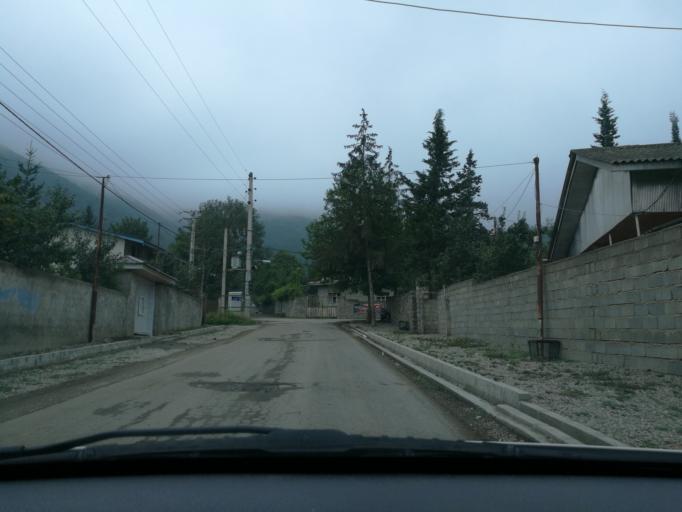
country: IR
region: Mazandaran
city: `Abbasabad
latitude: 36.4973
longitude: 51.2169
